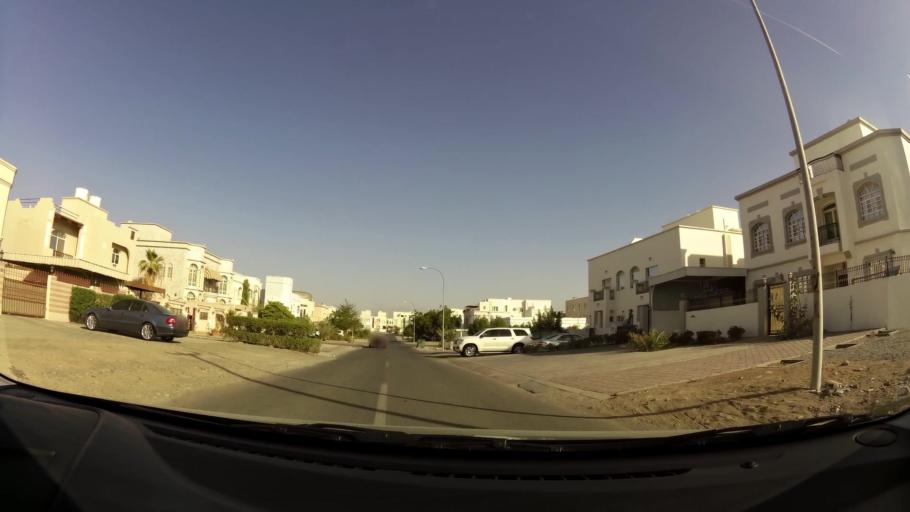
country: OM
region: Muhafazat Masqat
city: As Sib al Jadidah
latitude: 23.5982
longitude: 58.2084
